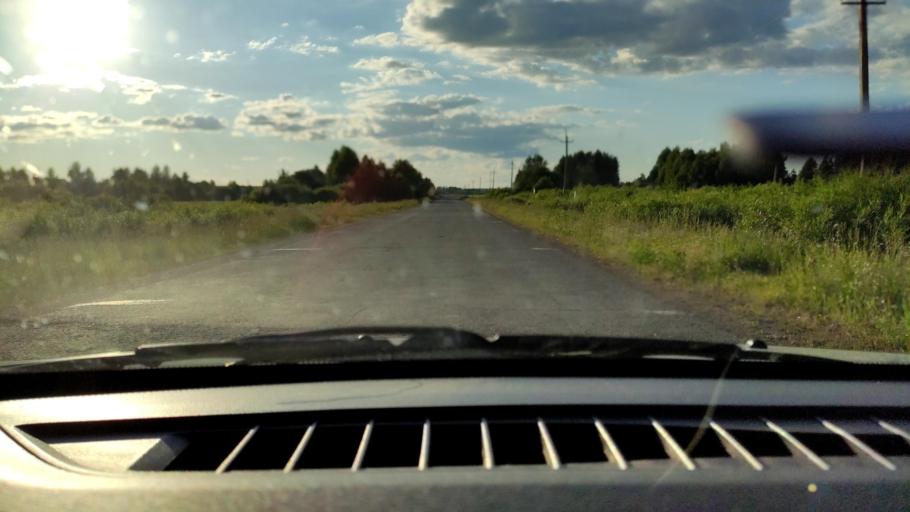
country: RU
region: Perm
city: Uinskoye
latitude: 57.0944
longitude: 56.5504
